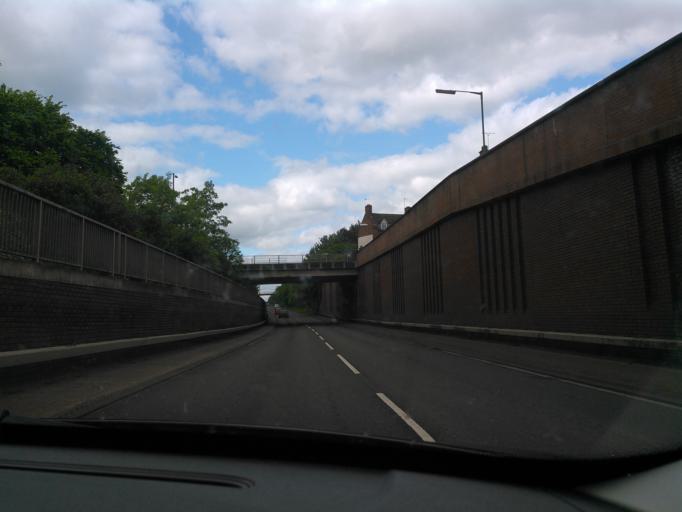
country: GB
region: England
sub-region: Shropshire
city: Shrewsbury
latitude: 52.7049
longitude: -2.7358
